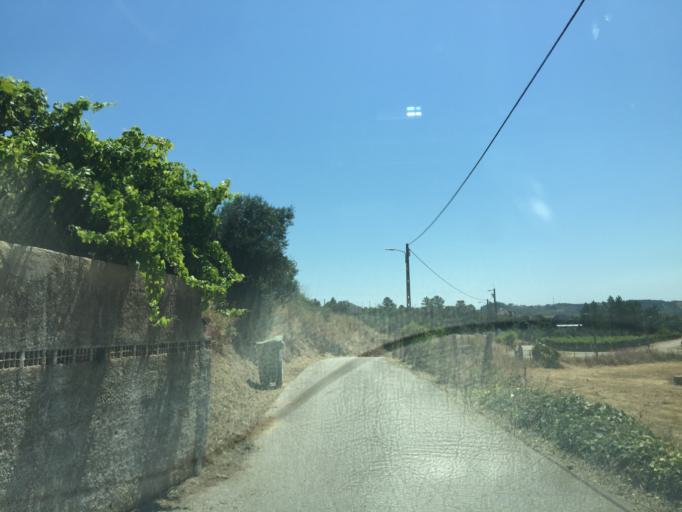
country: PT
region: Santarem
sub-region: Tomar
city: Tomar
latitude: 39.5756
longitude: -8.3005
